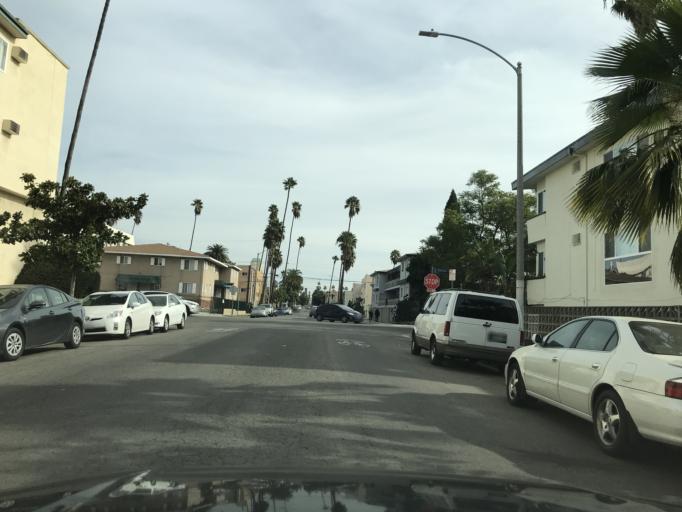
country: US
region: California
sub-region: Los Angeles County
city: Hollywood
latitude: 34.0671
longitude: -118.3121
